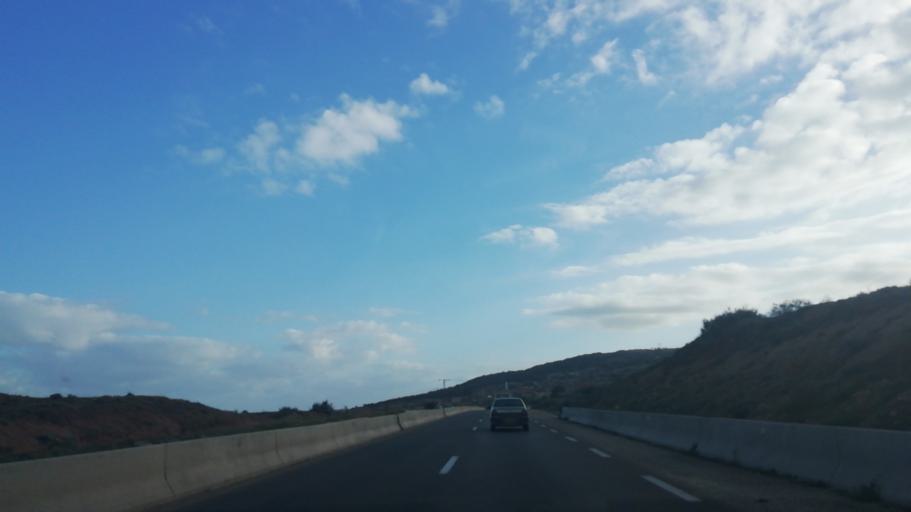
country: DZ
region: Mostaganem
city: Mostaganem
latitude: 36.0955
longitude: 0.2071
